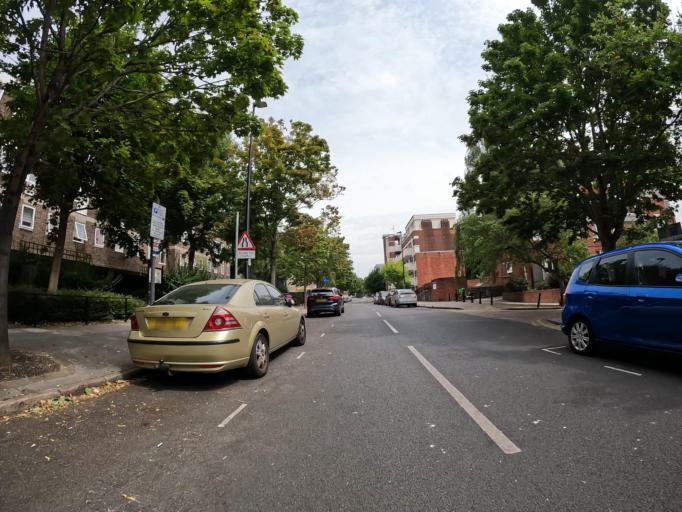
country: GB
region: England
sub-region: Greater London
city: Poplar
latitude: 51.5087
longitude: -0.0146
